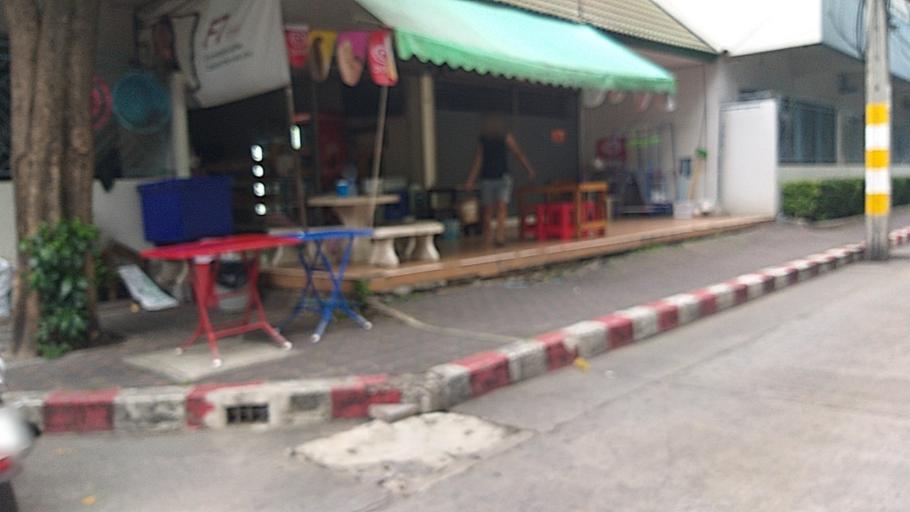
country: TH
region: Bangkok
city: Bang Na
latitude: 13.6681
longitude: 100.6808
